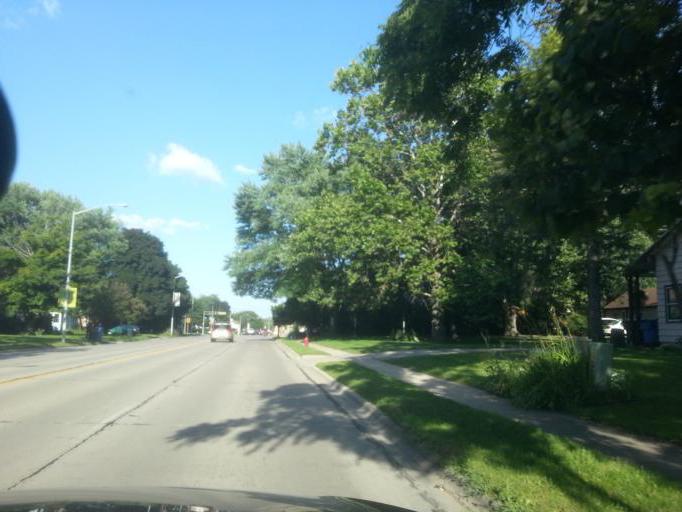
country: US
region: Wisconsin
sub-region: Dane County
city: Middleton
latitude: 43.0970
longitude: -89.5039
